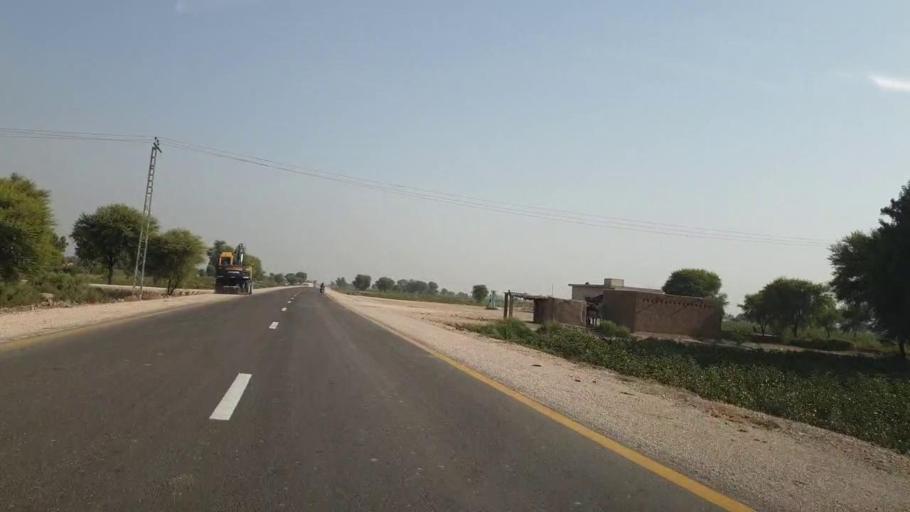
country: PK
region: Sindh
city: Sehwan
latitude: 26.4753
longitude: 67.7874
